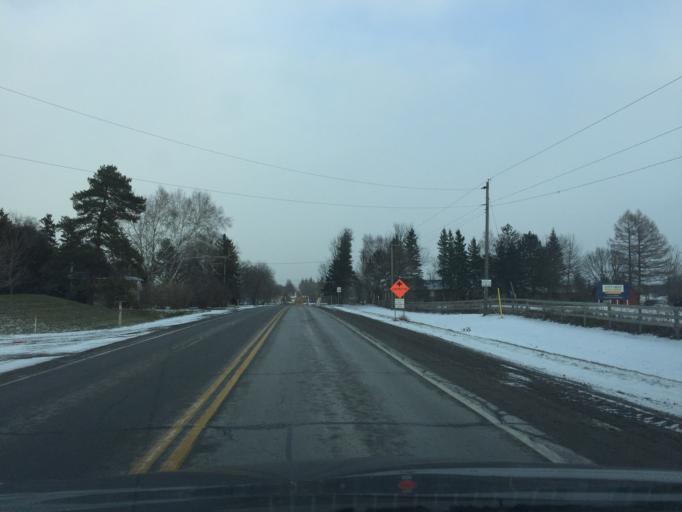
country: CA
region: Ontario
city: Uxbridge
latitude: 44.0767
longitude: -78.9880
